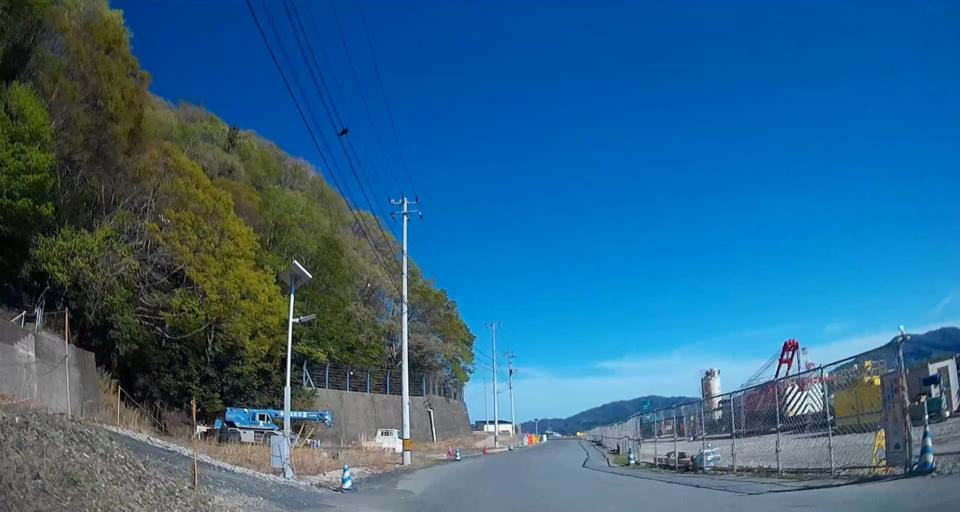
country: JP
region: Iwate
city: Kamaishi
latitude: 39.2727
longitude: 141.8944
